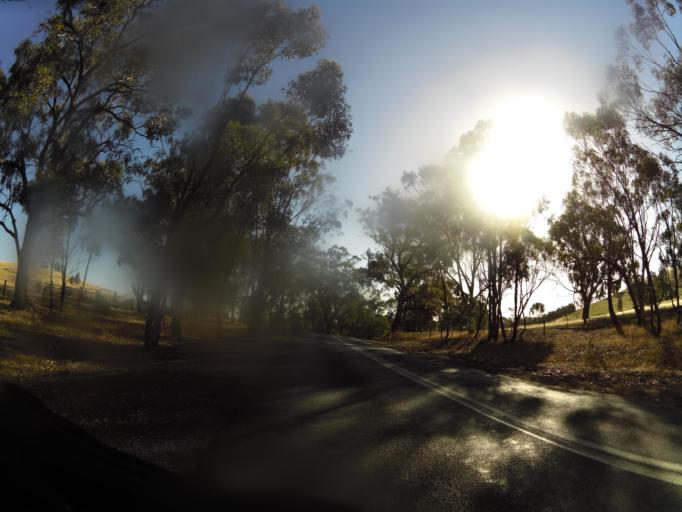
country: AU
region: Victoria
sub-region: Murrindindi
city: Kinglake West
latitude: -37.0101
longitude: 145.1227
